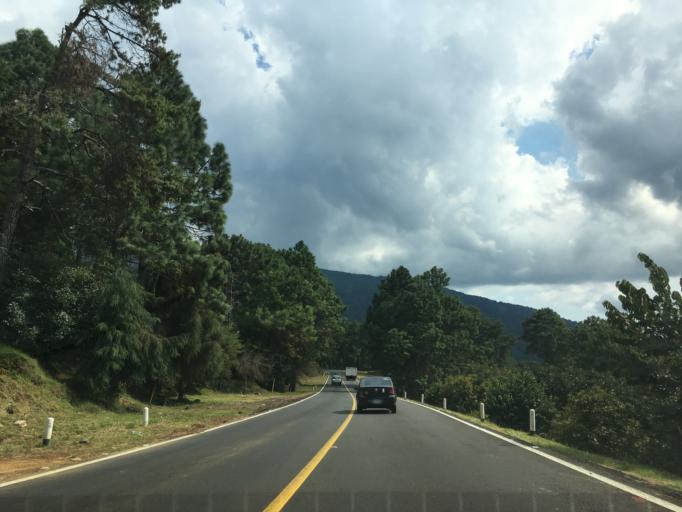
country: MX
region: Michoacan
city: Tingambato
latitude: 19.4967
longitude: -101.8353
